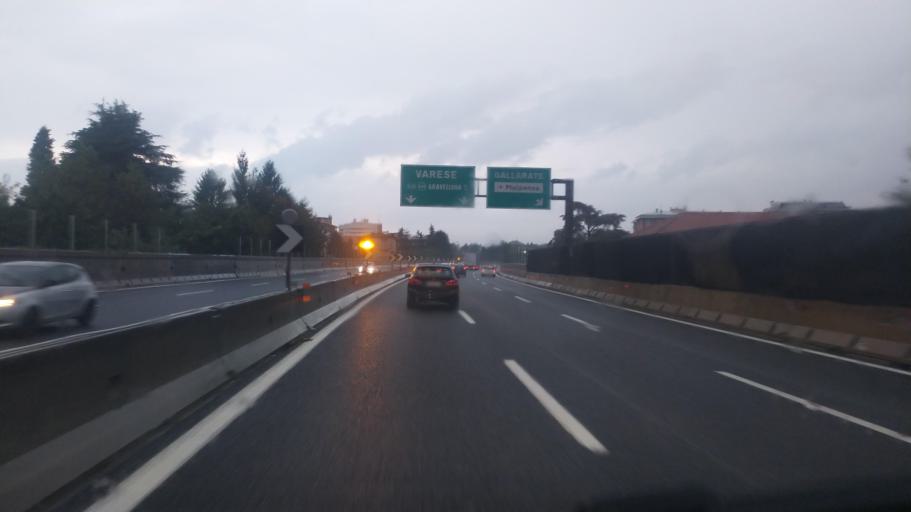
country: IT
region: Lombardy
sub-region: Provincia di Varese
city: Gallarate
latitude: 45.6633
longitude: 8.8021
